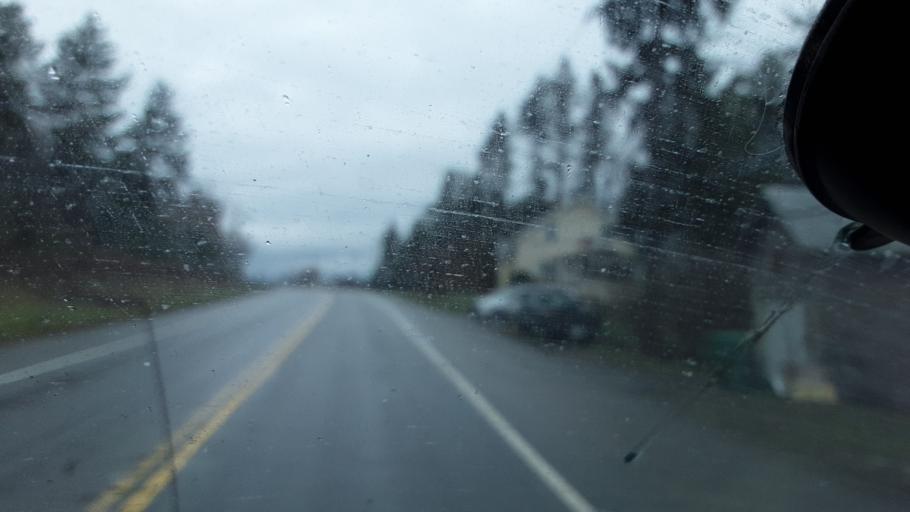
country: US
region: New York
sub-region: Cattaraugus County
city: Yorkshire
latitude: 42.5851
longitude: -78.4900
